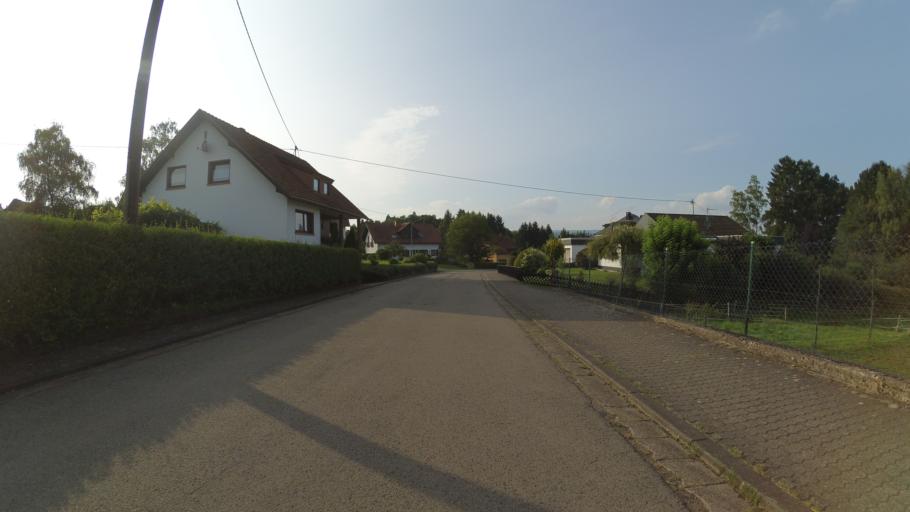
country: DE
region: Saarland
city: Wadern
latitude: 49.5351
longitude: 6.8889
